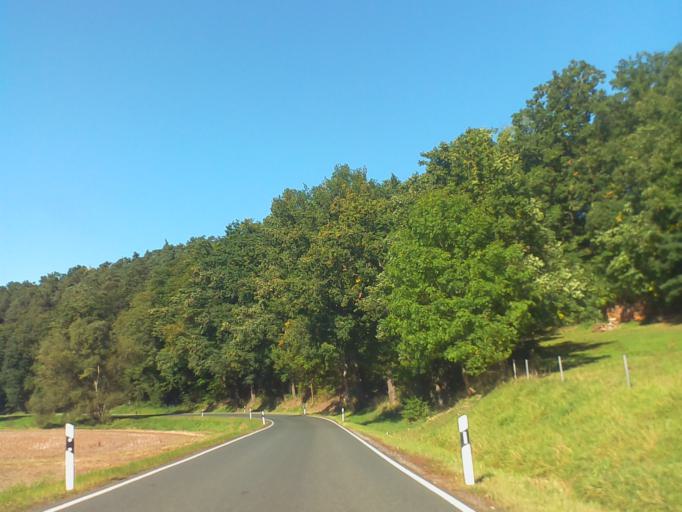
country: DE
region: Thuringia
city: Trobnitz
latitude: 50.8348
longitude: 11.7368
